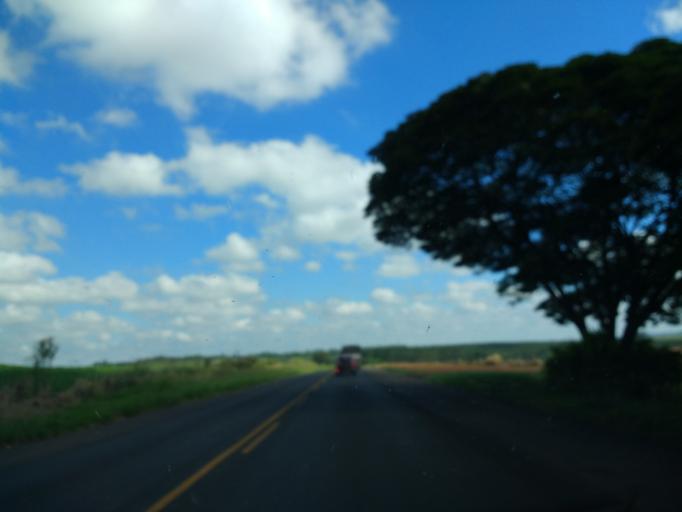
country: BR
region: Parana
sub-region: Umuarama
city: Umuarama
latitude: -23.8418
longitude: -53.3630
